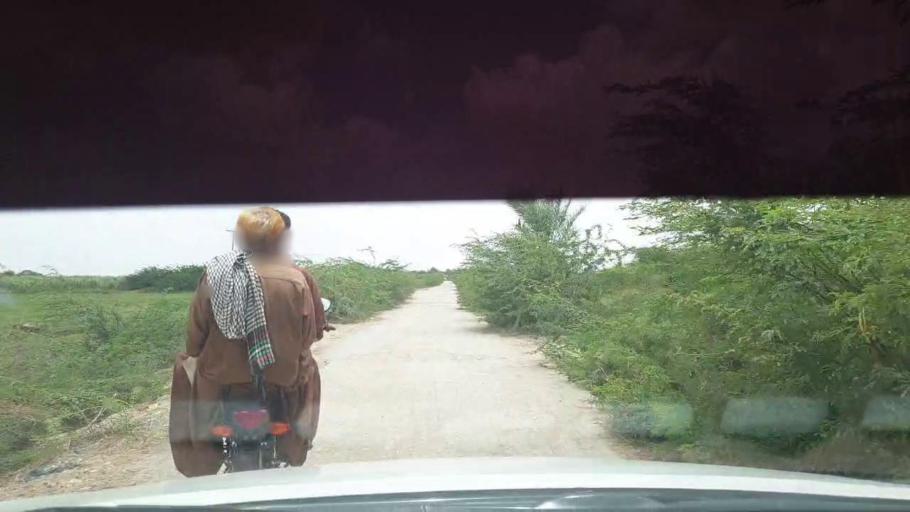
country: PK
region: Sindh
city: Kadhan
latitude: 24.4649
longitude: 69.0383
